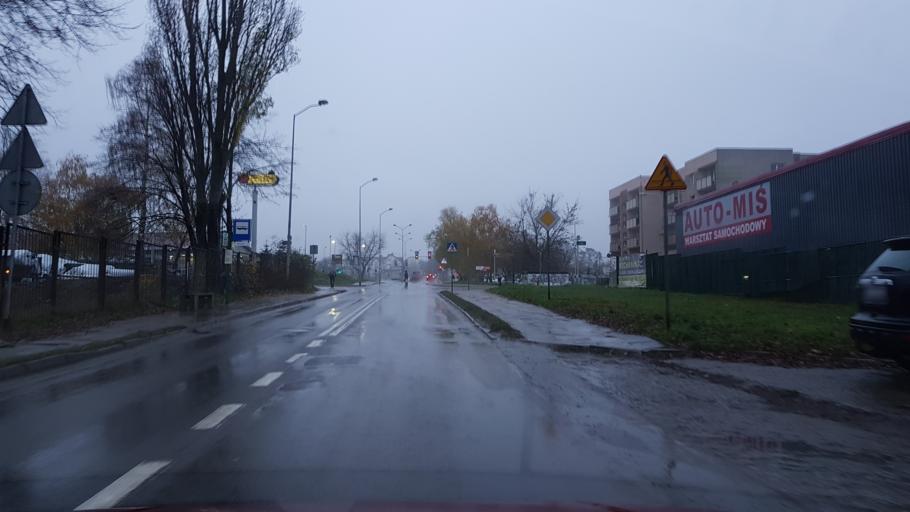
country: PL
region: West Pomeranian Voivodeship
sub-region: Szczecin
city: Szczecin
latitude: 53.4602
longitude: 14.5562
